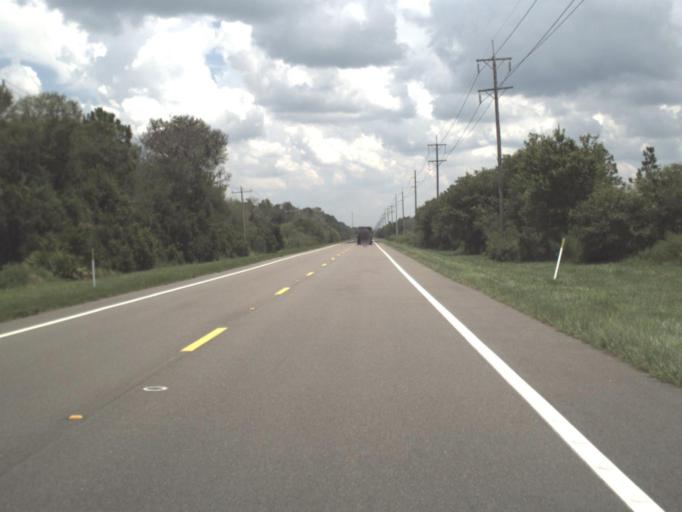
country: US
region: Florida
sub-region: Hillsborough County
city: Boyette
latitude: 27.7045
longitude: -82.1044
